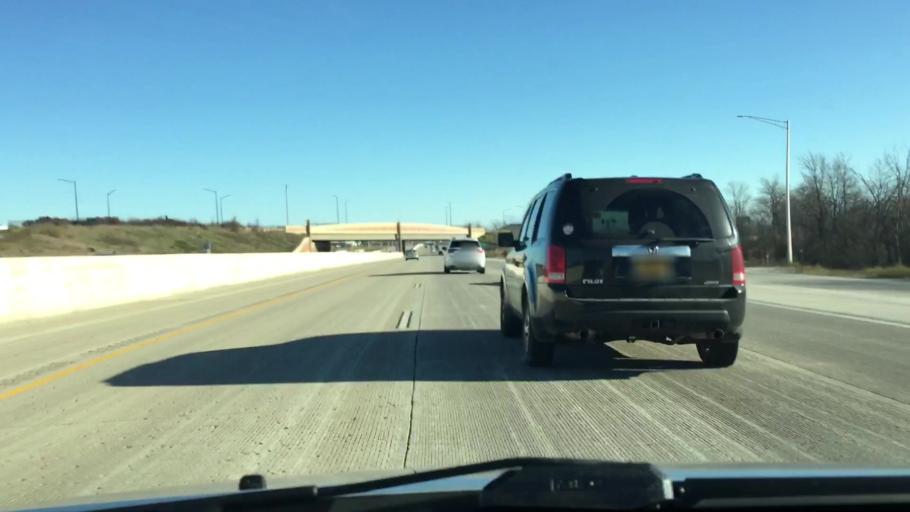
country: US
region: Wisconsin
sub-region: Brown County
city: De Pere
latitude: 44.4288
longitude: -88.1149
